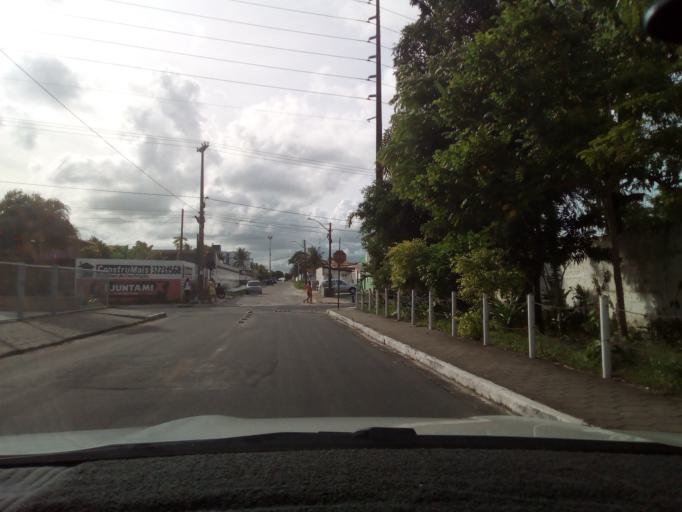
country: BR
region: Paraiba
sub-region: Joao Pessoa
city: Joao Pessoa
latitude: -7.1559
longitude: -34.8767
